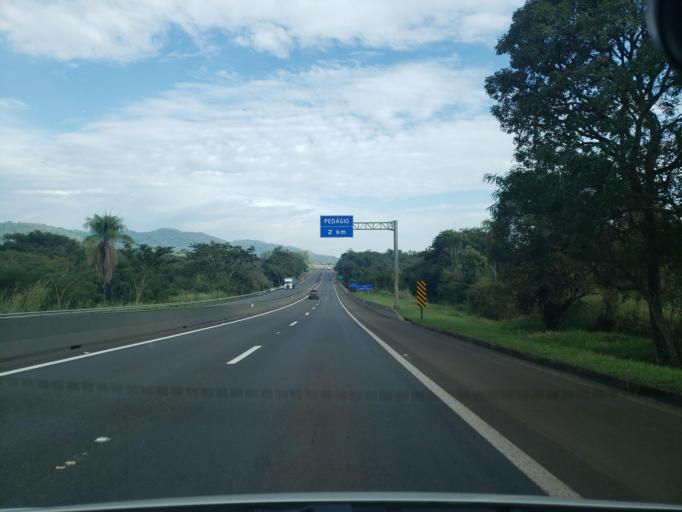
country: BR
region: Sao Paulo
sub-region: Brotas
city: Brotas
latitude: -22.2637
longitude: -48.2263
